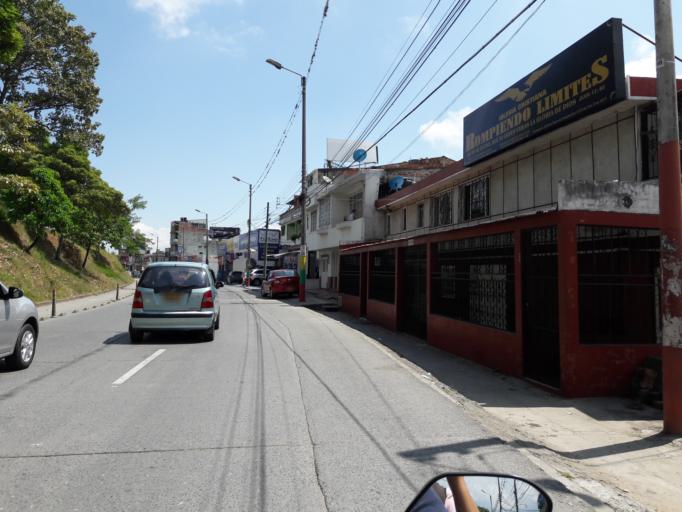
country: CO
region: Tolima
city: Ibague
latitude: 4.4352
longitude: -75.2200
